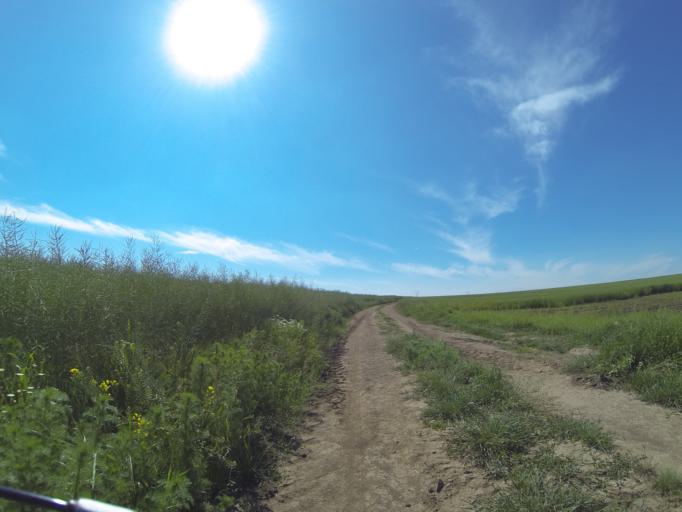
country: RO
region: Dolj
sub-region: Comuna Leu
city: Leu
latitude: 44.2550
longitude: 24.0114
